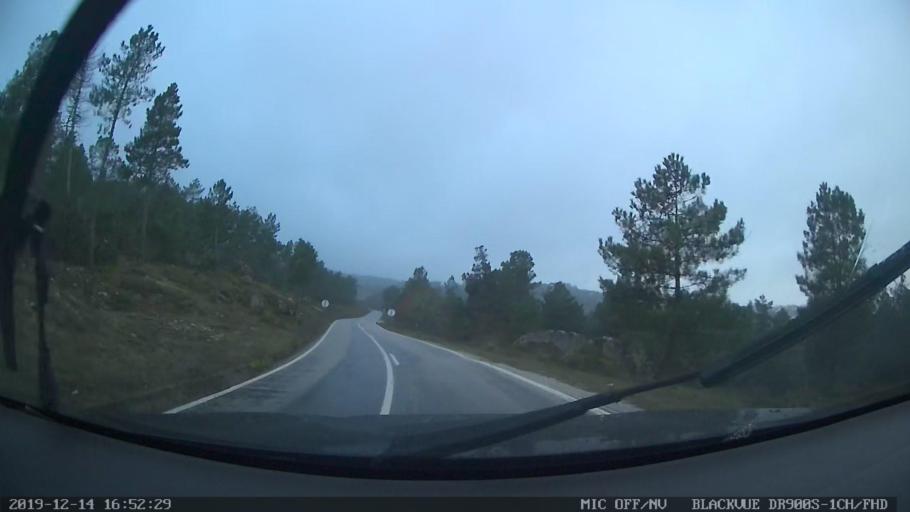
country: PT
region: Vila Real
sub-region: Murca
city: Murca
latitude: 41.4271
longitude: -7.5097
